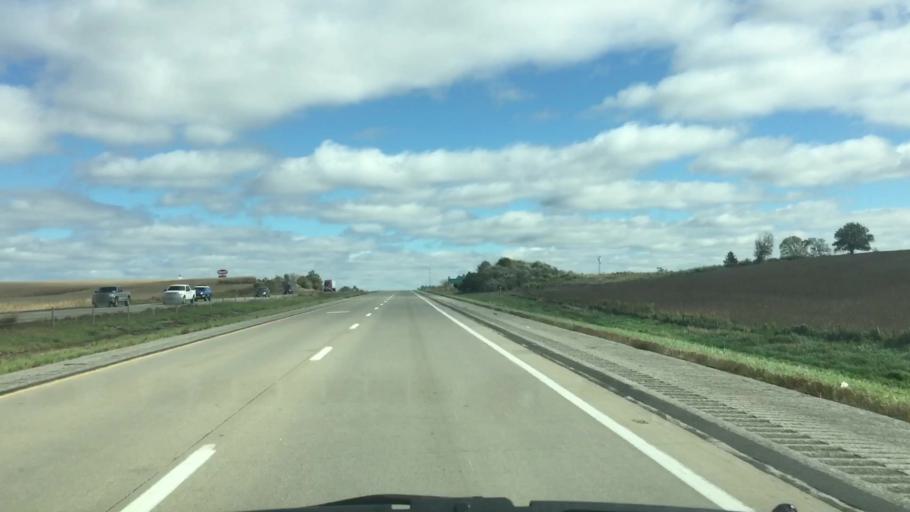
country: US
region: Iowa
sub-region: Iowa County
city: Williamsburg
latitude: 41.6898
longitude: -92.0784
